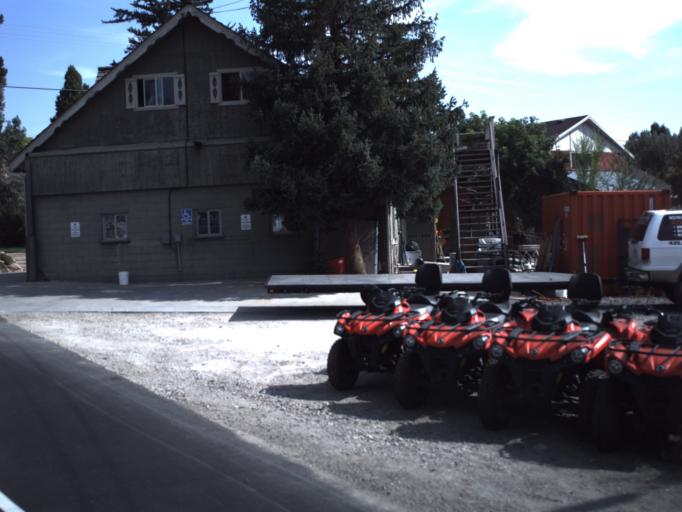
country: US
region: Utah
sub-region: Wasatch County
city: Midway
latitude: 40.5117
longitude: -111.4723
